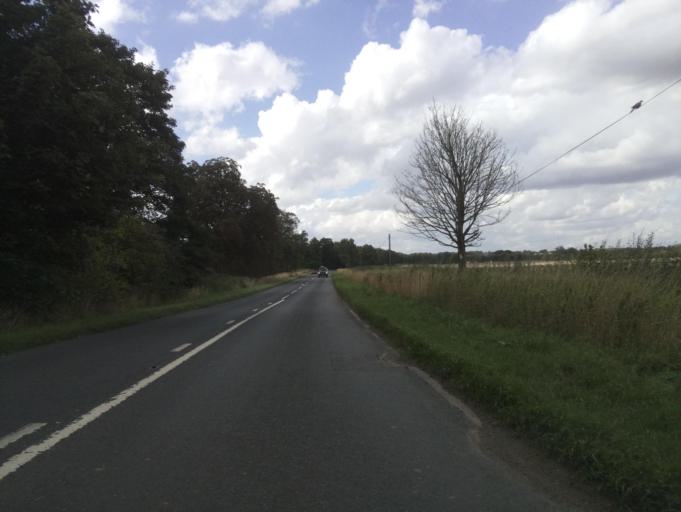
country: GB
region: England
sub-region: North Yorkshire
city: Ripon
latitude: 54.1944
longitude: -1.5737
